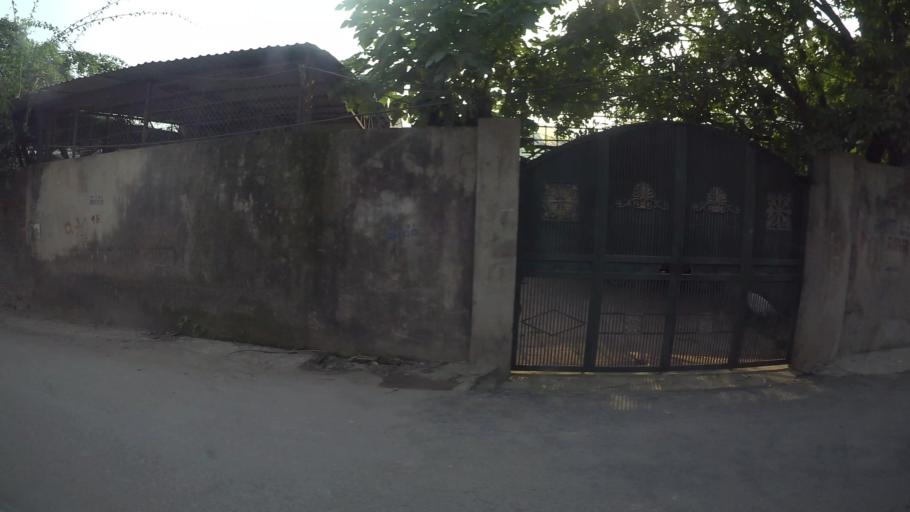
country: VN
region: Ha Noi
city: Ha Dong
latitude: 20.9972
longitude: 105.7435
